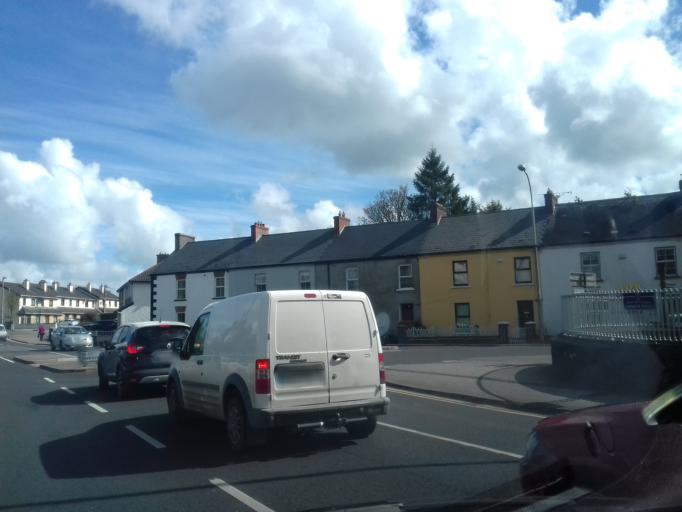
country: IE
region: Ulster
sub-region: An Cabhan
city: Cavan
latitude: 53.9947
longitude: -7.3605
